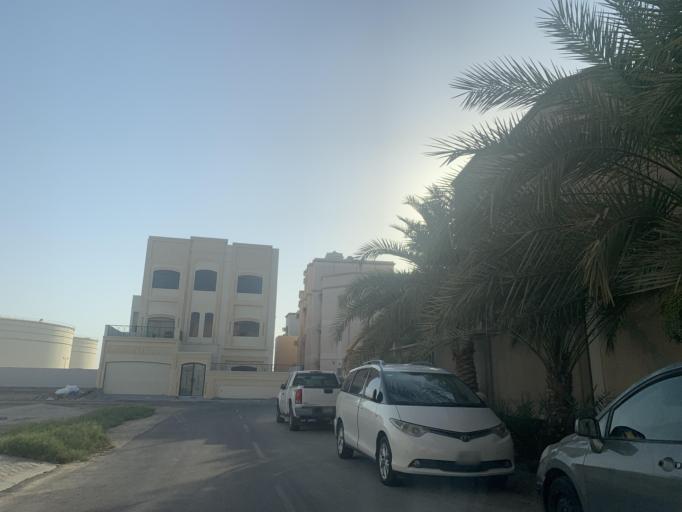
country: BH
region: Manama
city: Jidd Hafs
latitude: 26.2098
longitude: 50.5285
